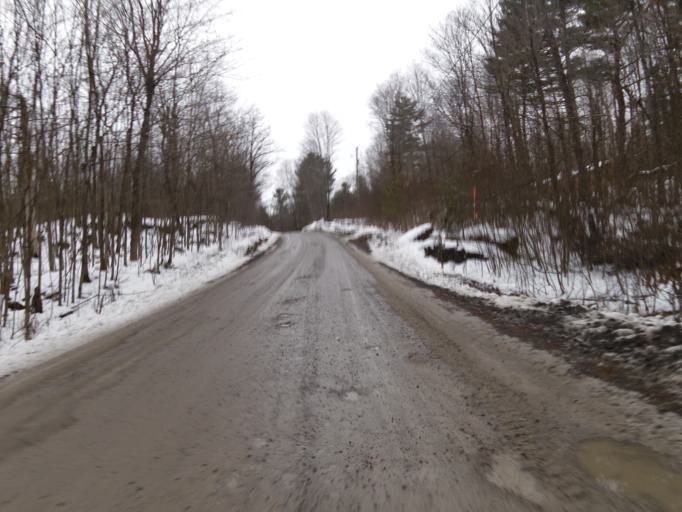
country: CA
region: Ontario
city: Carleton Place
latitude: 45.1765
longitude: -76.2283
